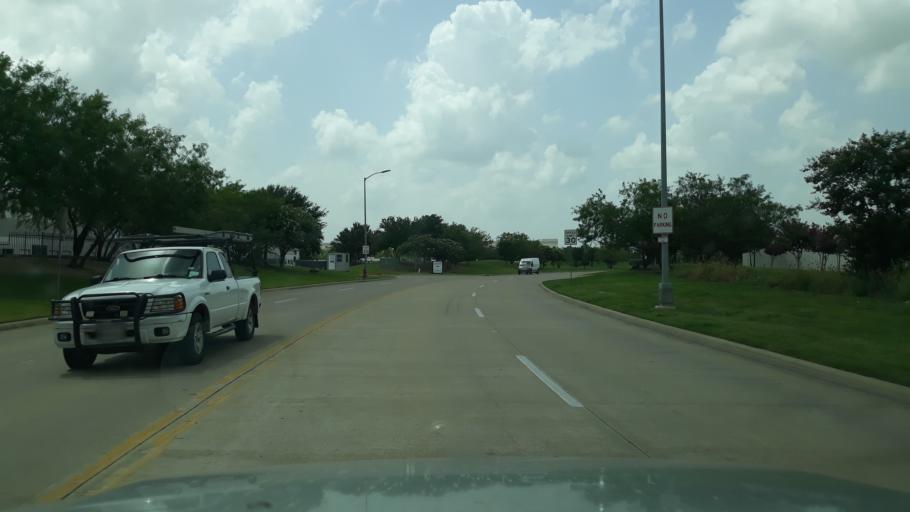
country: US
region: Texas
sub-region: Dallas County
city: Coppell
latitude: 32.9310
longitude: -97.0299
